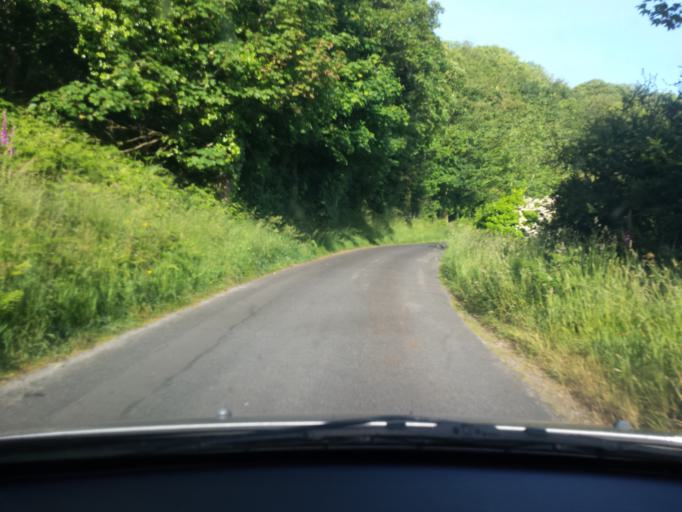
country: FR
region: Lower Normandy
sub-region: Departement de la Manche
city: Beaumont-Hague
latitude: 49.6853
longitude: -1.9243
